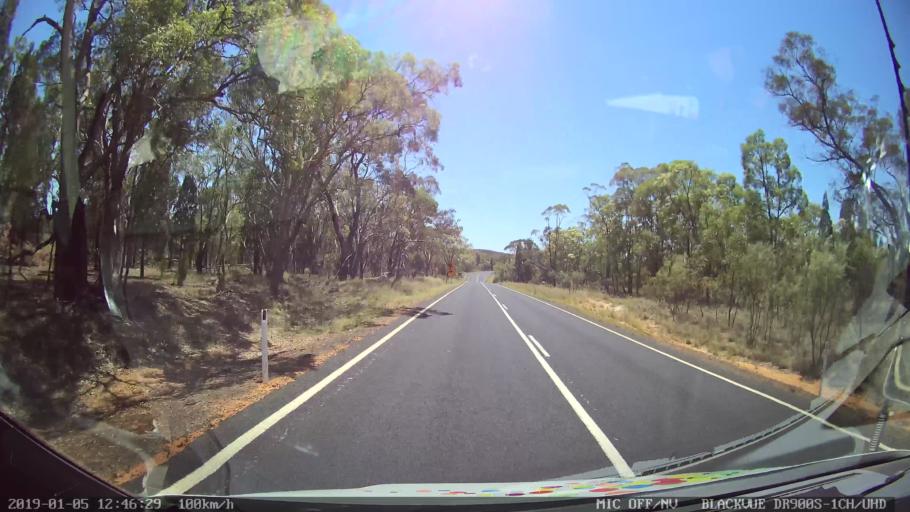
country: AU
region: New South Wales
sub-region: Warrumbungle Shire
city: Coonabarabran
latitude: -31.1175
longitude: 149.5631
